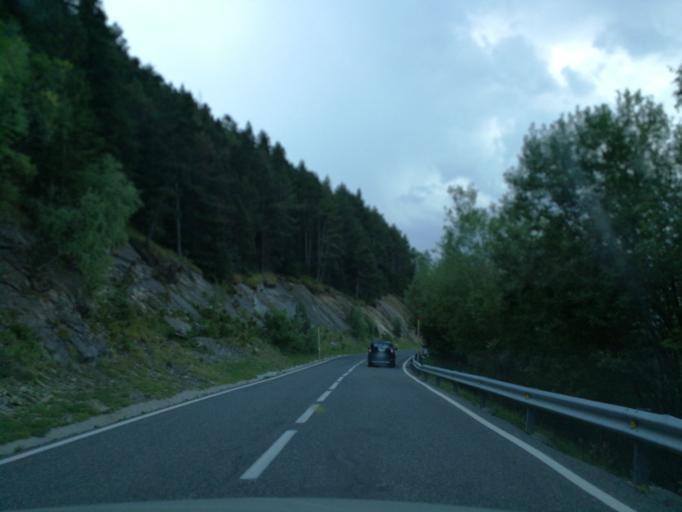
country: AD
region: Ordino
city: Ordino
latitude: 42.5546
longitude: 1.5511
